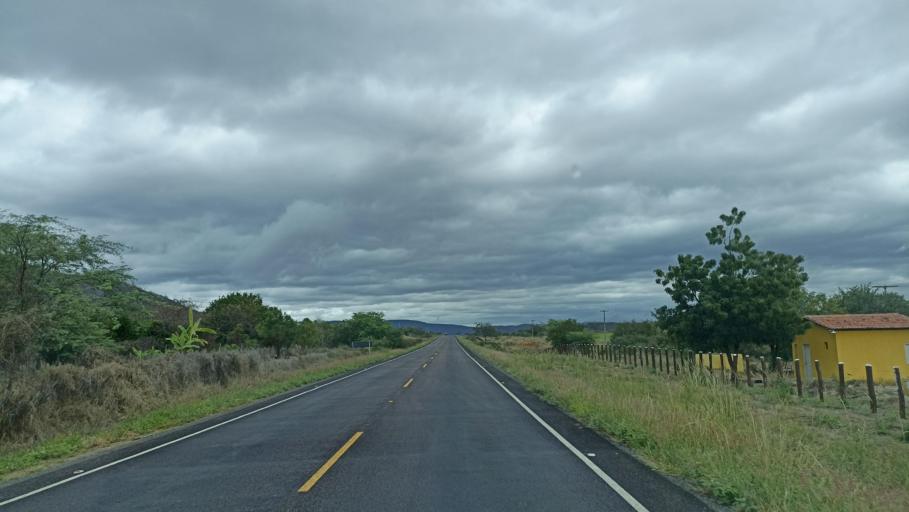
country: BR
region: Bahia
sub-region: Iacu
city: Iacu
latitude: -12.8933
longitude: -40.3979
